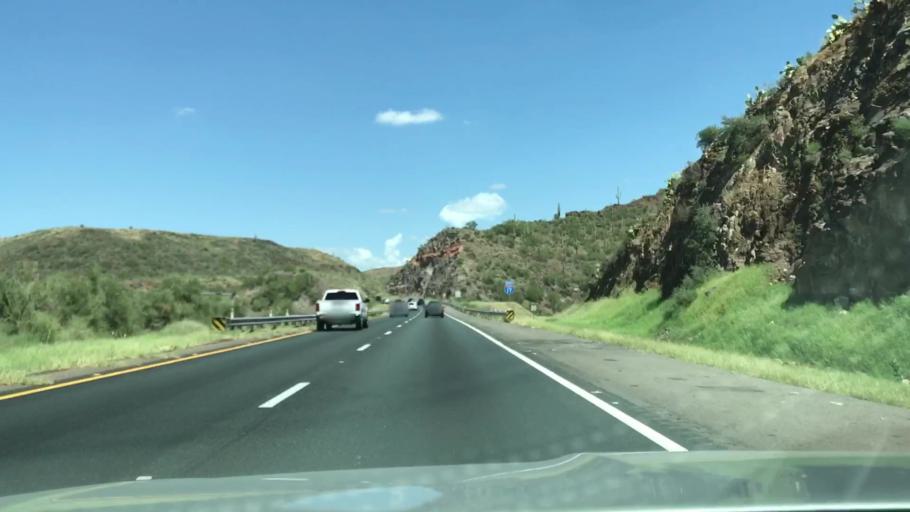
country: US
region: Arizona
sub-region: Yavapai County
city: Black Canyon City
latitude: 34.1420
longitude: -112.1421
